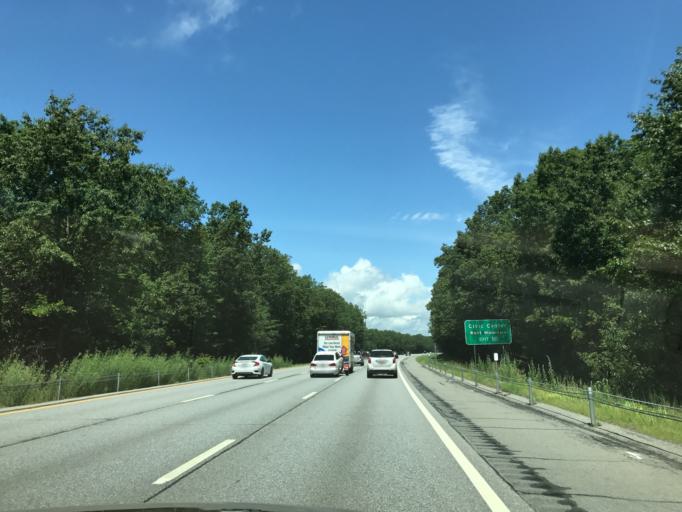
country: US
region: New York
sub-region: Warren County
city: West Glens Falls
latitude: 43.2832
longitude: -73.6800
